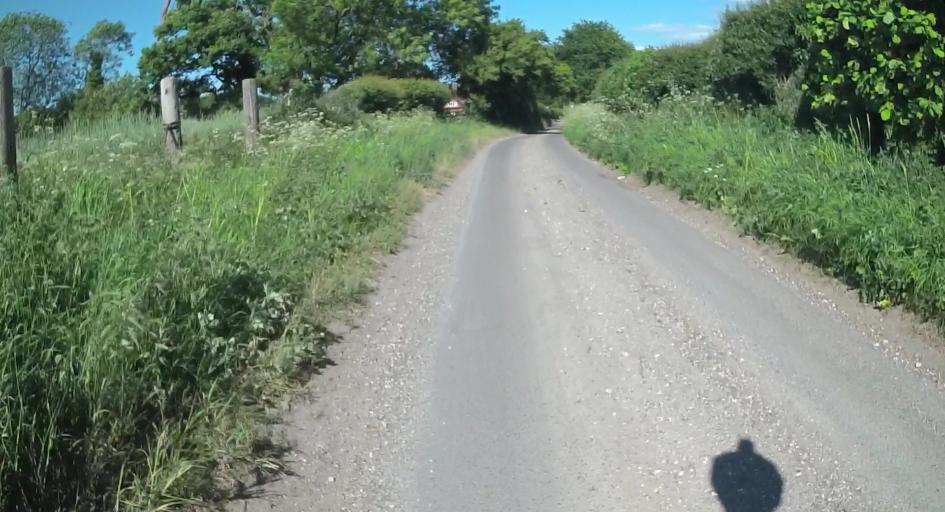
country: GB
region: England
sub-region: Hampshire
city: Old Basing
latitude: 51.2185
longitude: -1.0216
